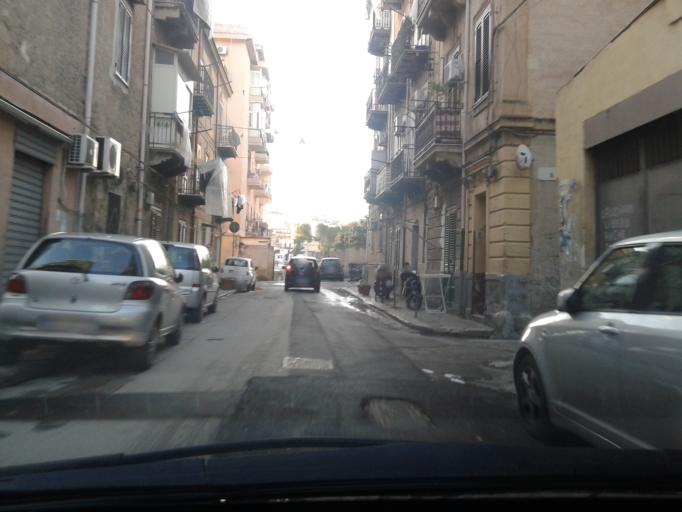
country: IT
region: Sicily
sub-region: Palermo
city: Palermo
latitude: 38.1137
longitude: 13.3450
